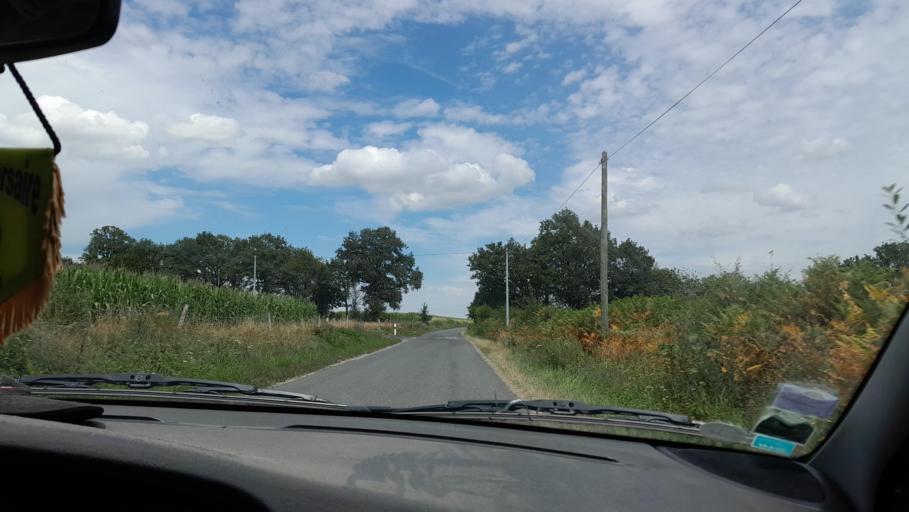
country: FR
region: Pays de la Loire
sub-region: Departement de la Mayenne
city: Saint-Pierre-la-Cour
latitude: 48.1560
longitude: -1.0321
